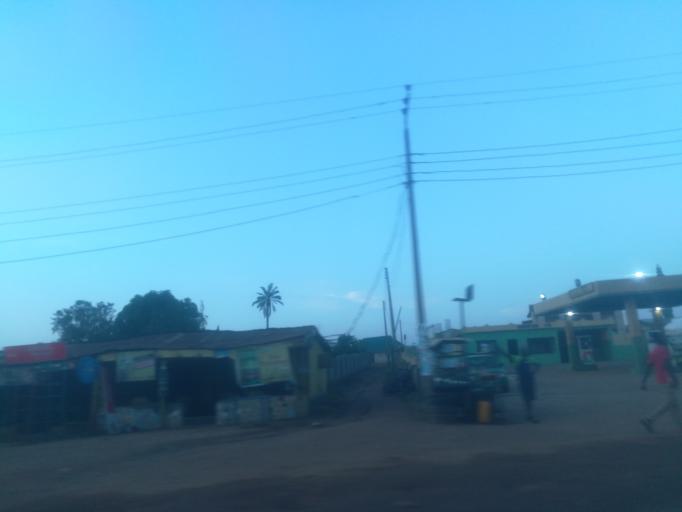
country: NG
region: Ogun
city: Abeokuta
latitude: 7.1784
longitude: 3.3954
